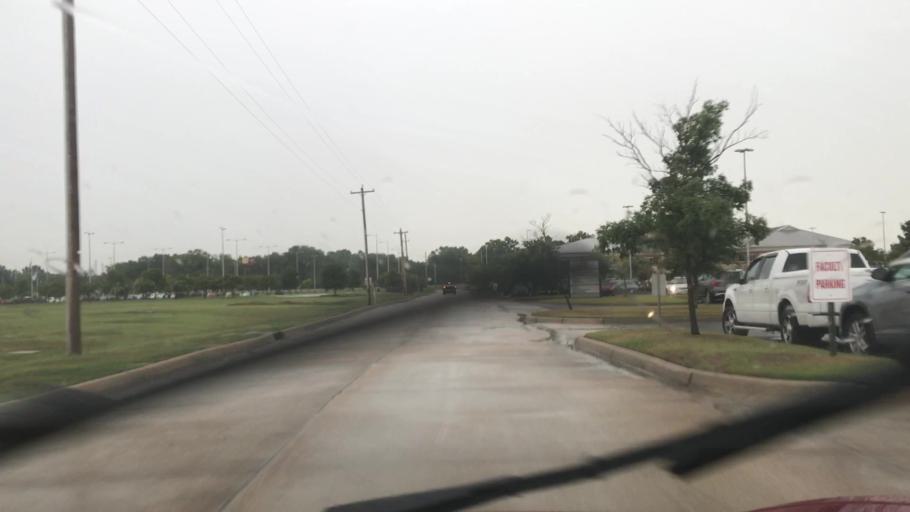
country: US
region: Louisiana
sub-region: Bossier Parish
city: Red Chute
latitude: 32.5398
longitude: -93.6449
